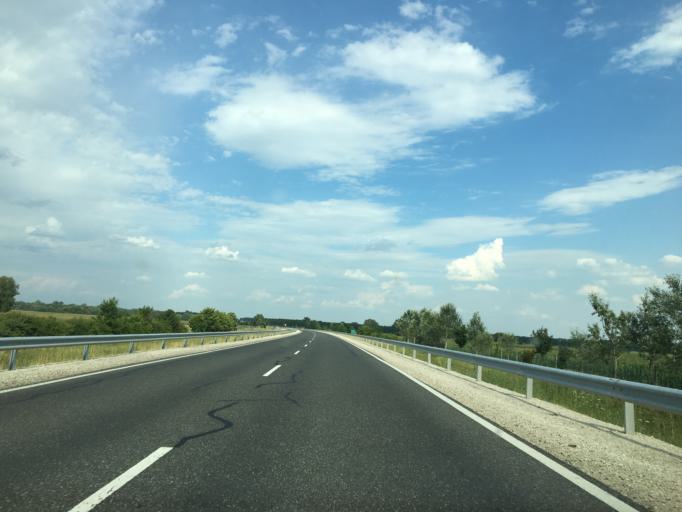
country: HU
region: Tolna
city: Bogyiszlo
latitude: 46.3516
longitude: 18.8659
